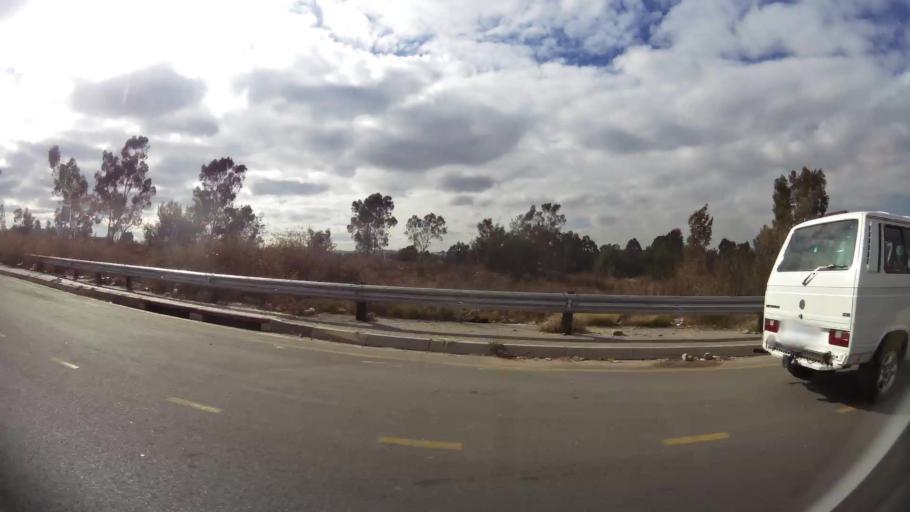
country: ZA
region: Gauteng
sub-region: City of Johannesburg Metropolitan Municipality
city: Roodepoort
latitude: -26.1945
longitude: 27.9024
